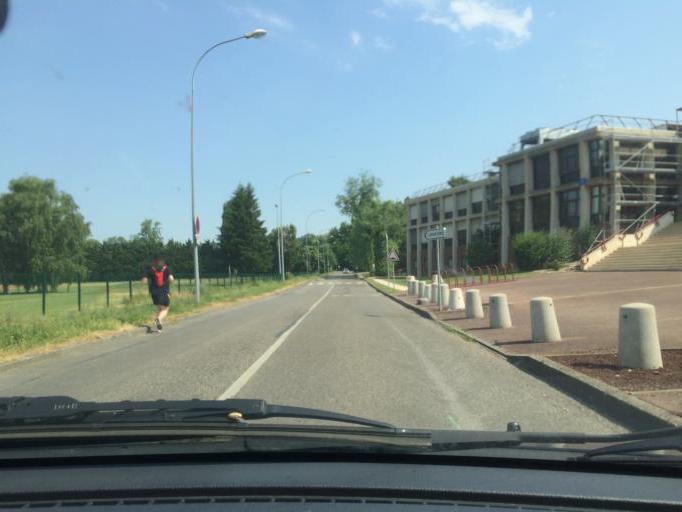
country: FR
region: Rhone-Alpes
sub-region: Departement du Rhone
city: Villeurbanne
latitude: 45.7822
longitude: 4.8649
